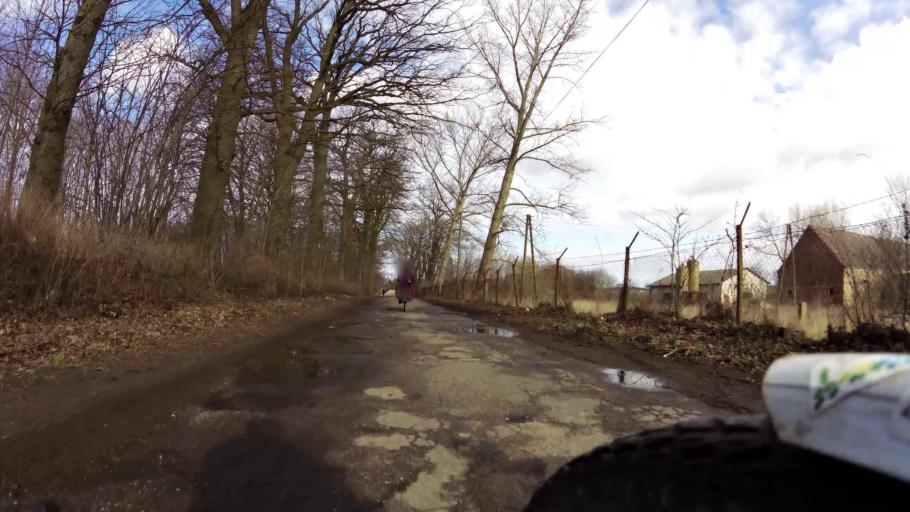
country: PL
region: West Pomeranian Voivodeship
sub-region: Powiat kamienski
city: Kamien Pomorski
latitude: 53.9920
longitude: 14.7690
